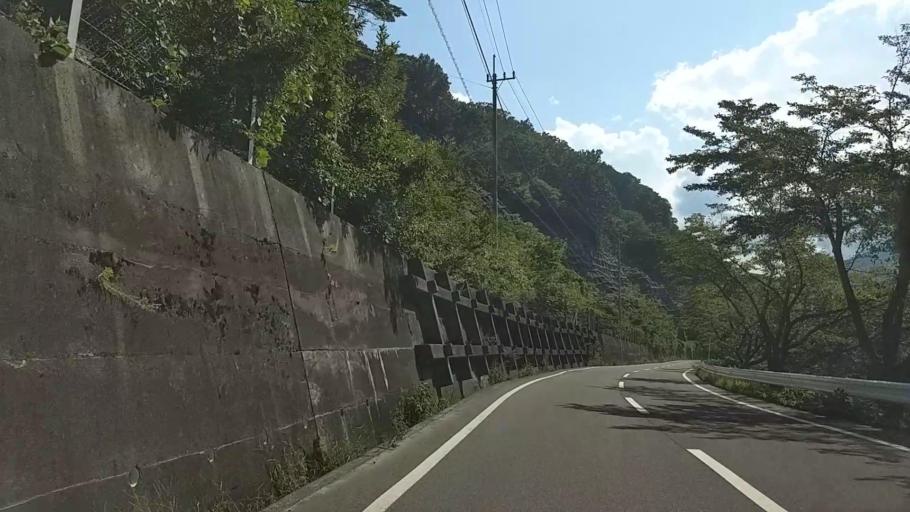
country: JP
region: Yamanashi
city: Fujikawaguchiko
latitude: 35.4051
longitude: 138.4551
